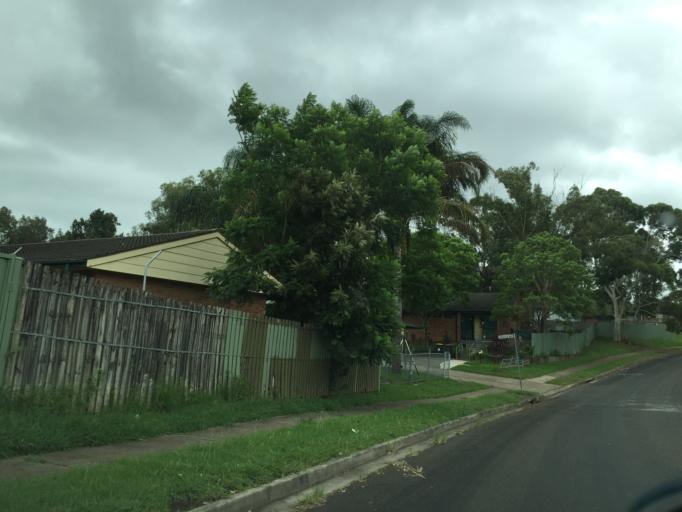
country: AU
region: New South Wales
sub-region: Blacktown
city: Blacktown
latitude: -33.7970
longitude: 150.9018
